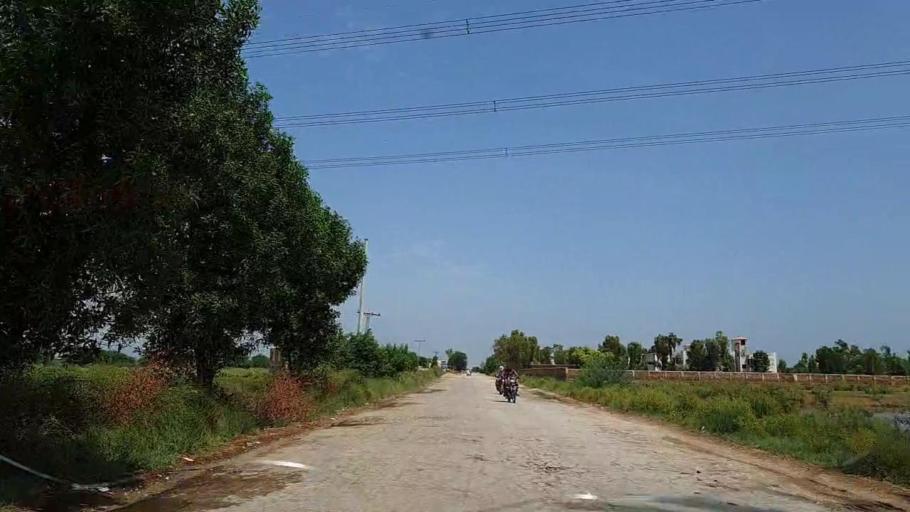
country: PK
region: Sindh
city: Naushahro Firoz
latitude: 26.8311
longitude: 68.1385
